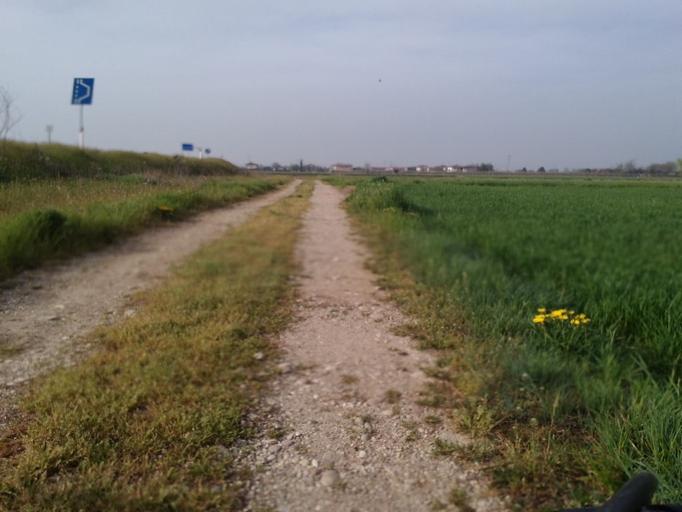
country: IT
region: Veneto
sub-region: Provincia di Verona
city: Villafranca di Verona
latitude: 45.3534
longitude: 10.8647
